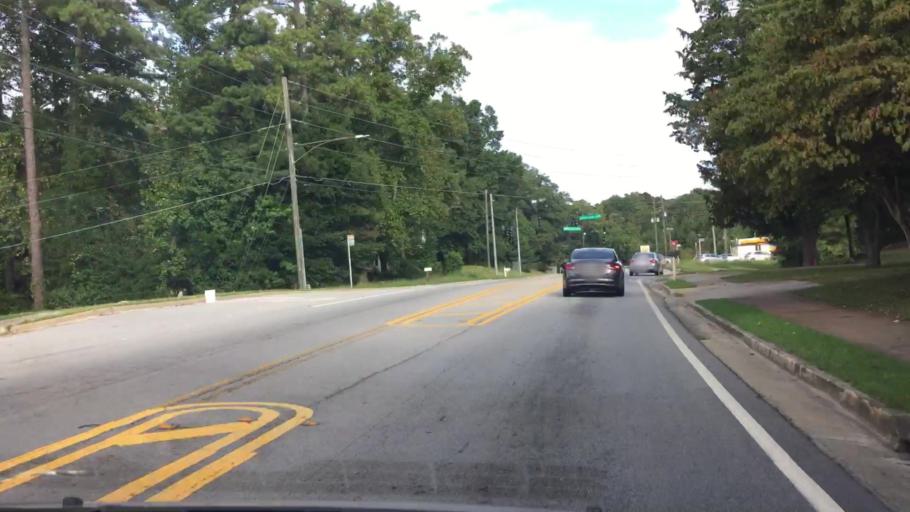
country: US
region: Georgia
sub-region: Clayton County
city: Conley
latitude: 33.6584
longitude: -84.2878
